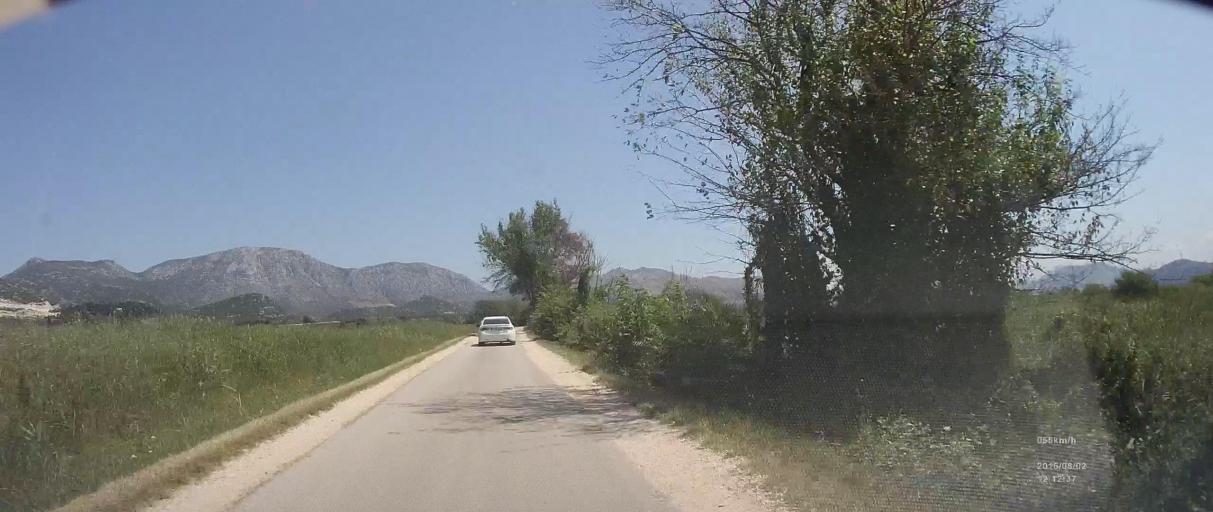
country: HR
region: Dubrovacko-Neretvanska
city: Komin
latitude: 43.0347
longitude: 17.4743
